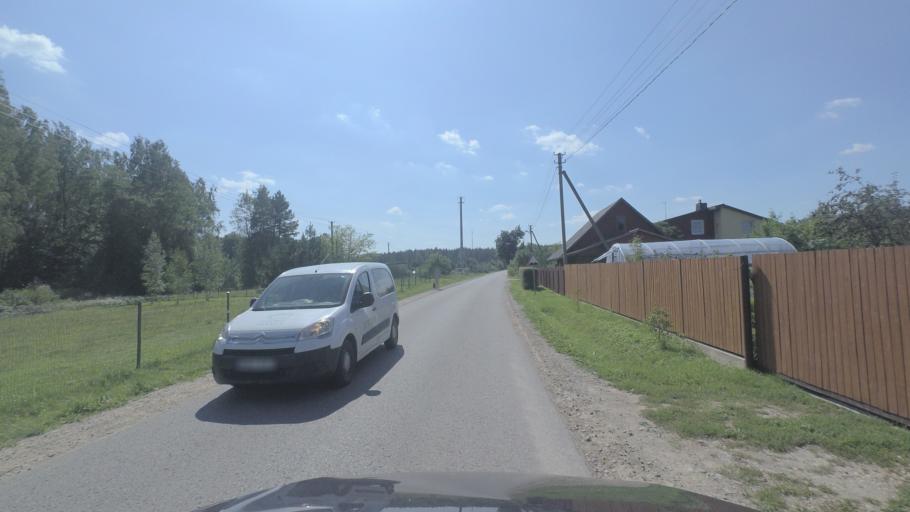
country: LT
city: Nemencine
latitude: 54.8302
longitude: 25.3656
